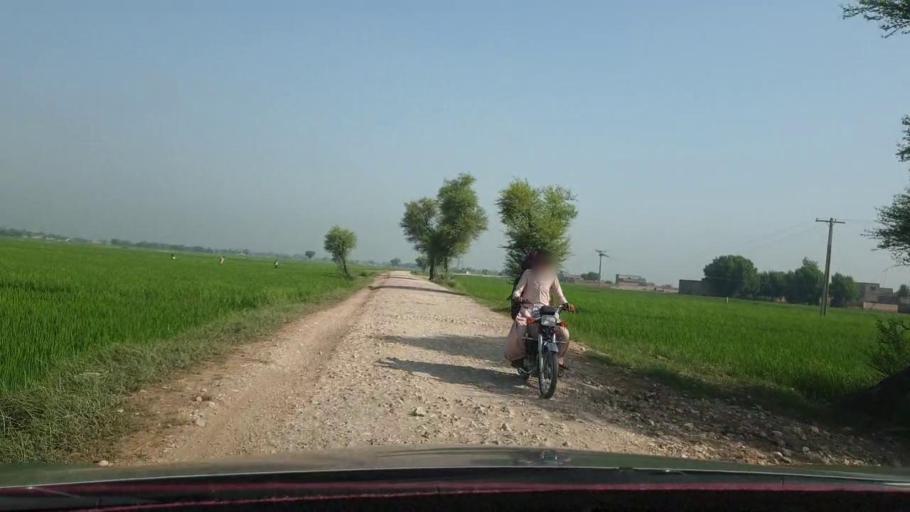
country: PK
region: Sindh
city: Nasirabad
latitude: 27.4821
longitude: 67.9256
